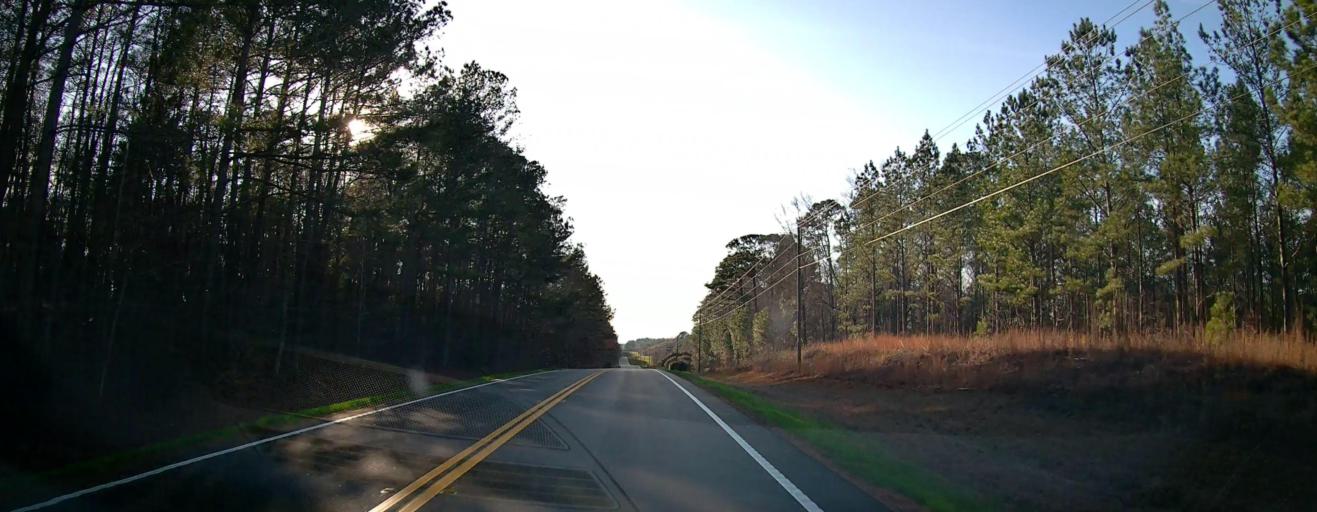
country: US
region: Georgia
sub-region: Harris County
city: Hamilton
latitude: 32.7473
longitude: -84.9988
